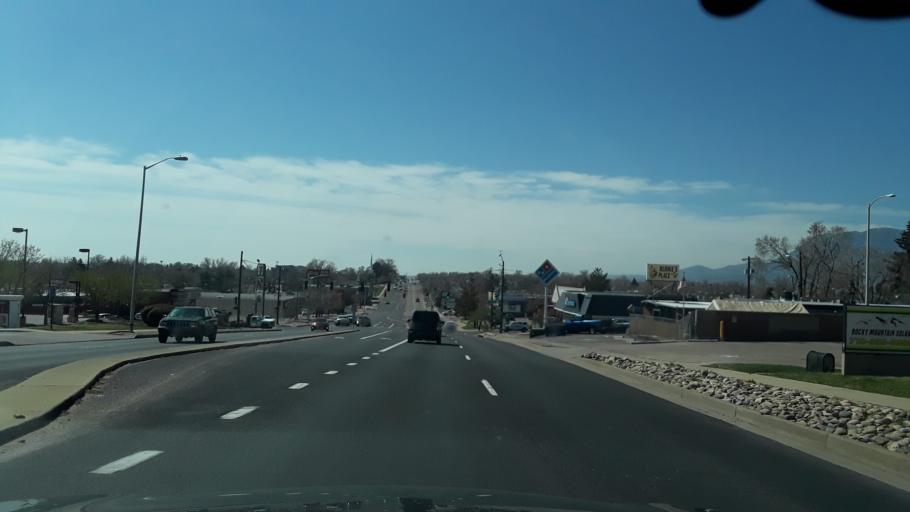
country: US
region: Colorado
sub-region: El Paso County
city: Colorado Springs
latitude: 38.8481
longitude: -104.7759
